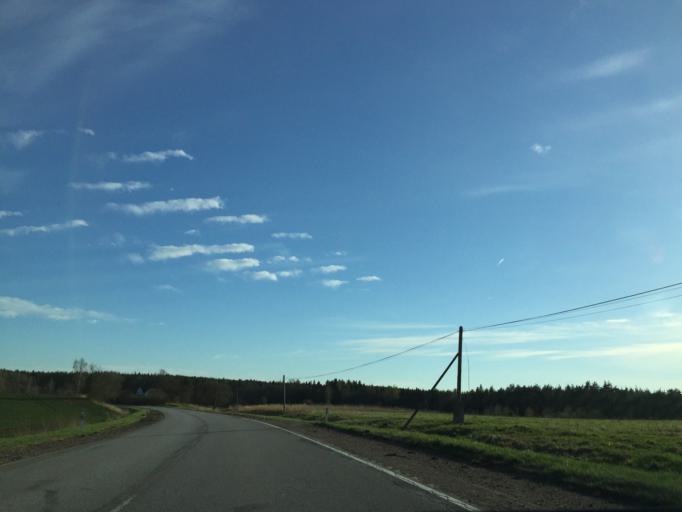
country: LV
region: Valkas Rajons
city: Valka
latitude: 57.7438
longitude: 25.9492
